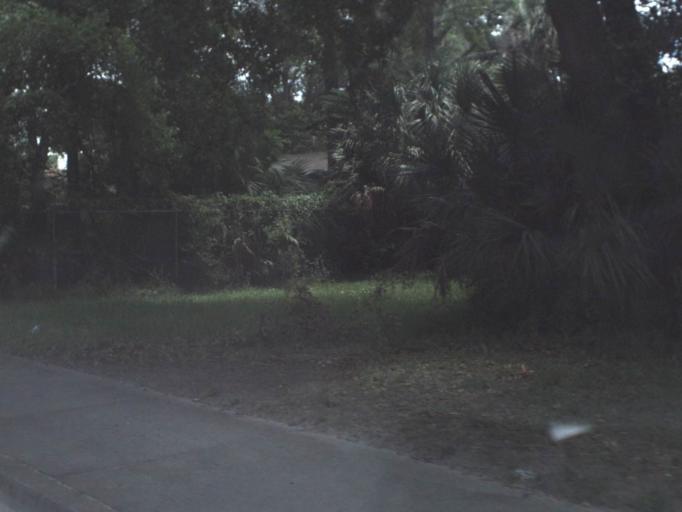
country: US
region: Florida
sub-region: Duval County
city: Jacksonville
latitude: 30.3093
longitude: -81.6491
